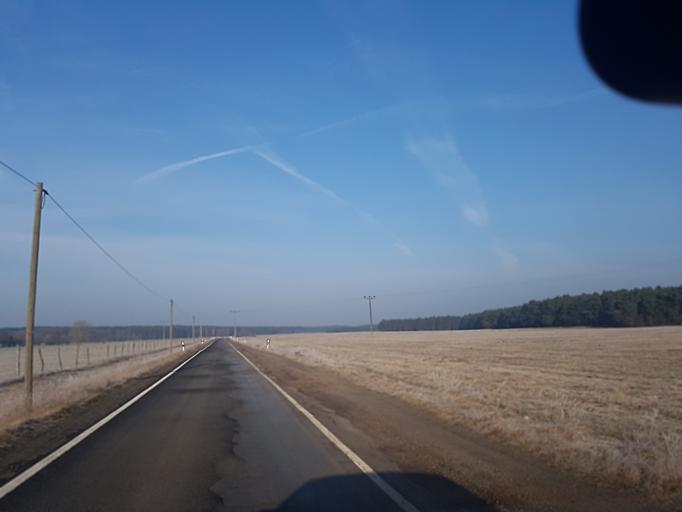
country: DE
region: Brandenburg
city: Wollin
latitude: 52.2509
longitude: 12.4790
